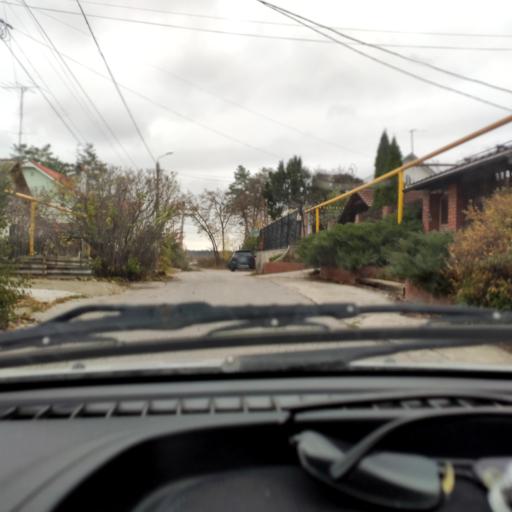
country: RU
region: Samara
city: Tol'yatti
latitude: 53.4802
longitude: 49.3576
